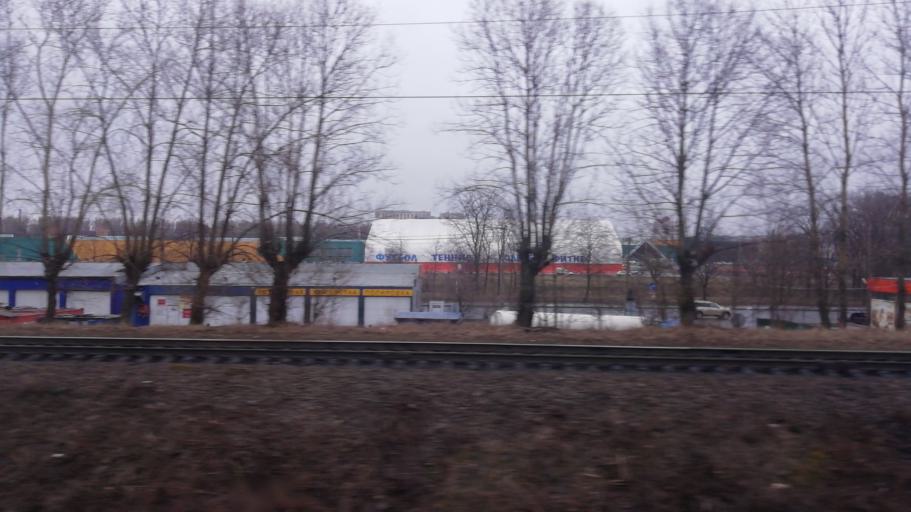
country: RU
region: St.-Petersburg
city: Kupchino
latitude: 59.8754
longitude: 30.3534
